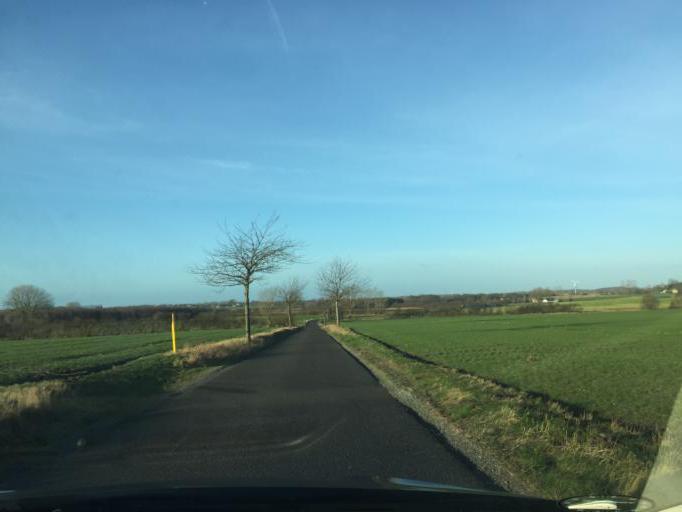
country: DK
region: South Denmark
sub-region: Middelfart Kommune
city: Ejby
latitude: 55.4429
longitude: 9.9401
